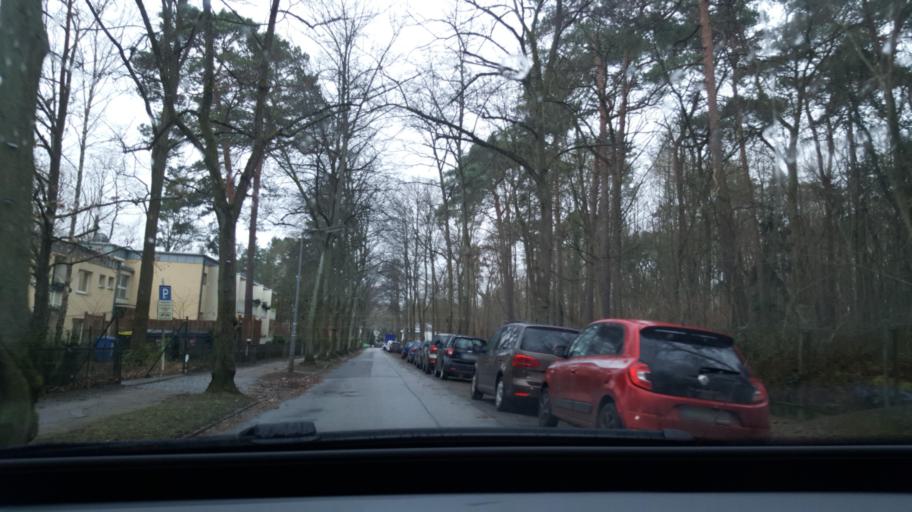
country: DE
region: Berlin
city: Wannsee
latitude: 52.4289
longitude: 13.1603
